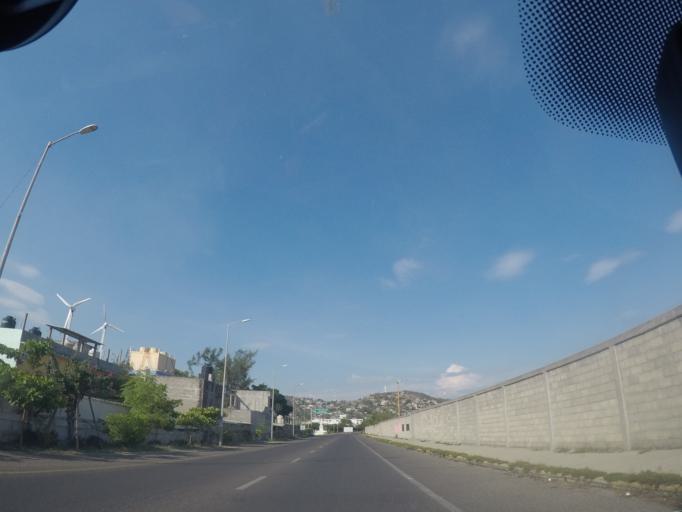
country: MX
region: Oaxaca
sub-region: Salina Cruz
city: Salina Cruz
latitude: 16.1739
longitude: -95.1968
